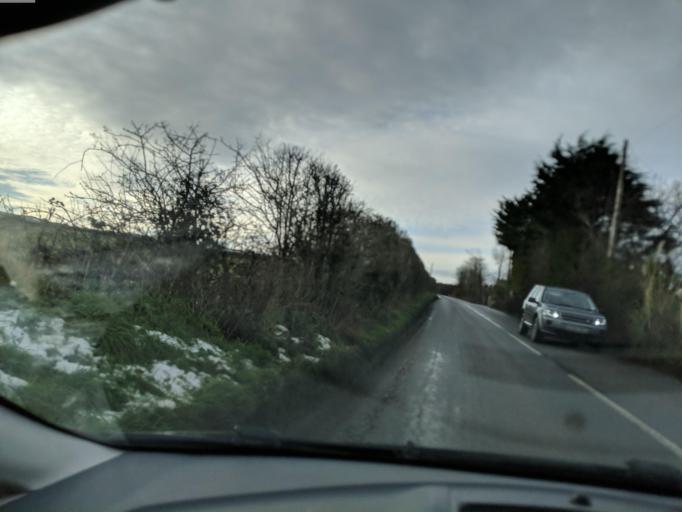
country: GB
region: England
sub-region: Cornwall
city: Jacobstow
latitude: 50.6748
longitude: -4.6108
